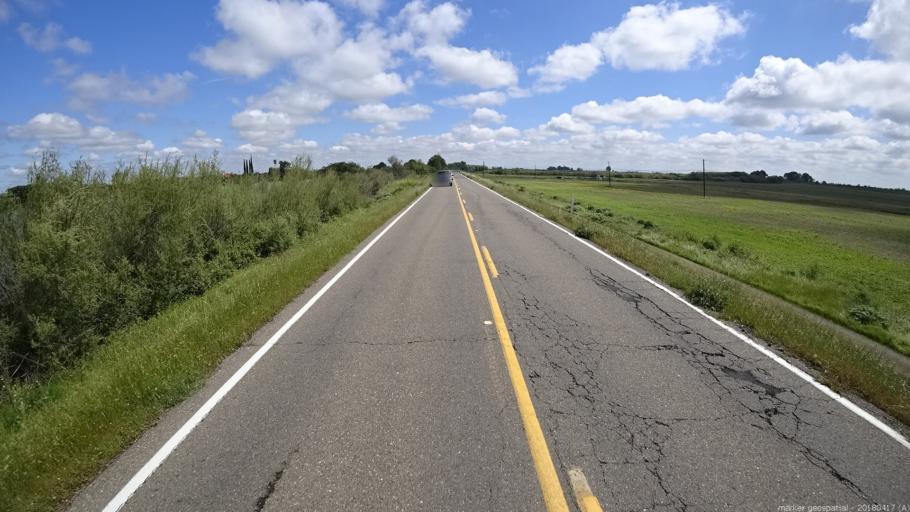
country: US
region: California
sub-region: Sacramento County
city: Walnut Grove
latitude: 38.1896
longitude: -121.5737
